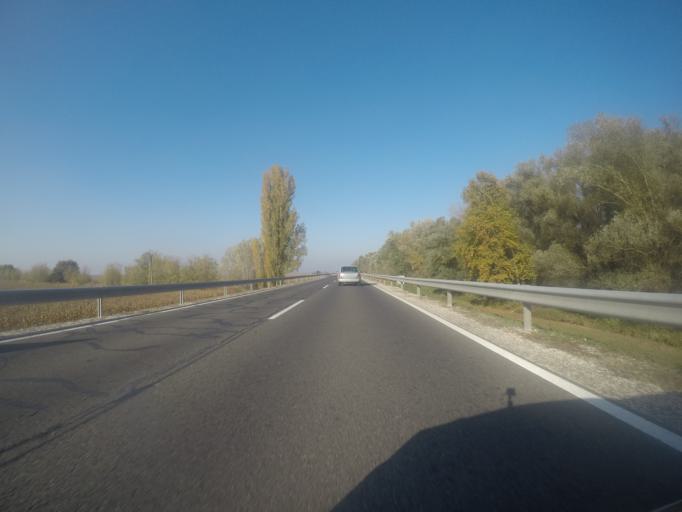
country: HU
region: Fejer
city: Ivancsa
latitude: 47.1891
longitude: 18.8708
